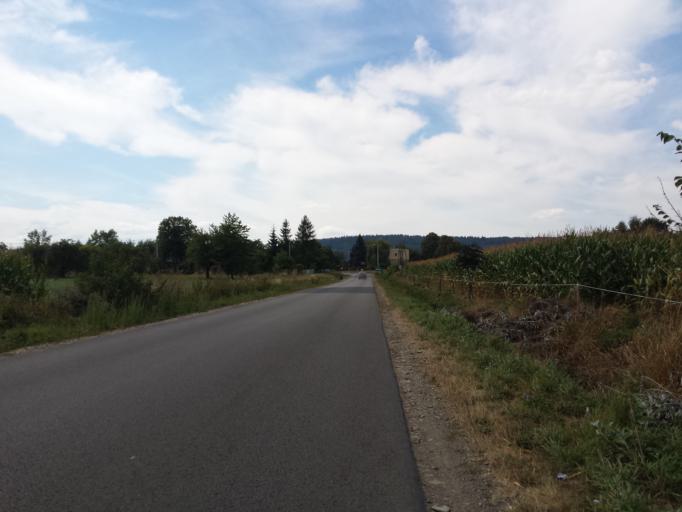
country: PL
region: Subcarpathian Voivodeship
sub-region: Powiat przemyski
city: Fredropol
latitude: 49.6996
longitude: 22.7494
